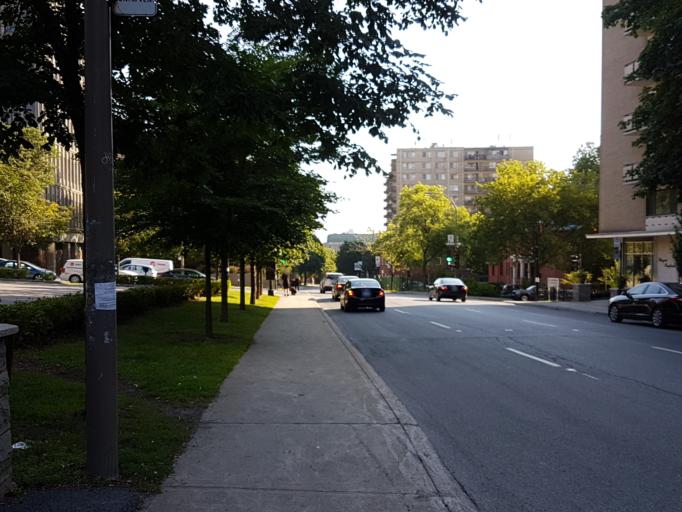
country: CA
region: Quebec
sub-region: Montreal
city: Montreal
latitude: 45.5015
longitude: -73.5815
